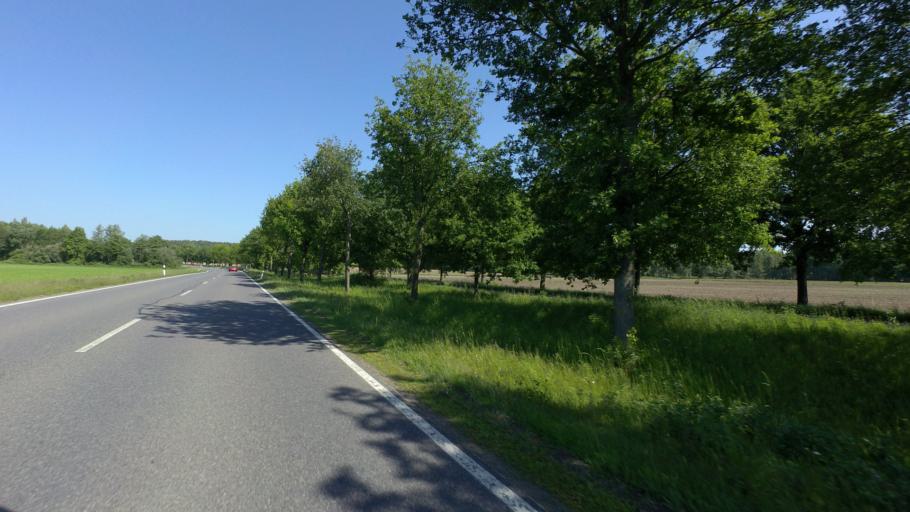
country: DE
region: Saxony
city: Kamenz
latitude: 51.2981
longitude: 14.1019
